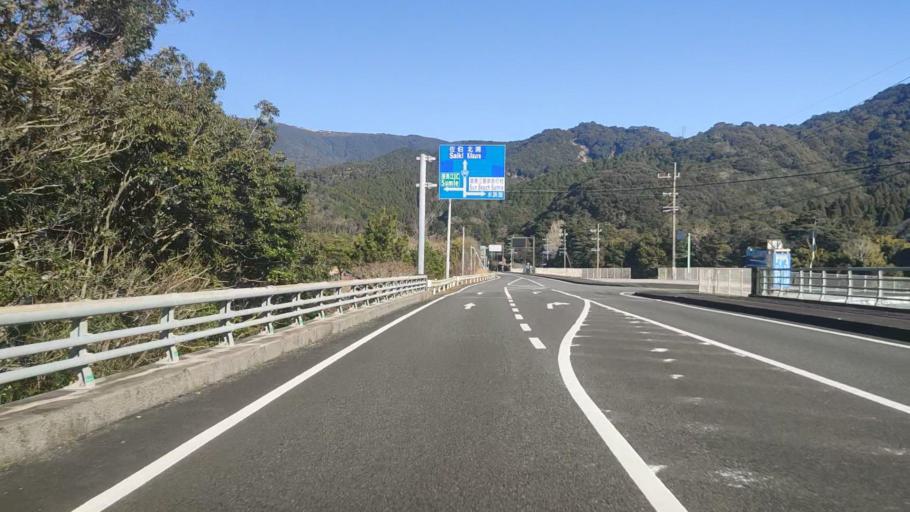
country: JP
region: Miyazaki
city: Nobeoka
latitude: 32.6629
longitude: 131.7665
